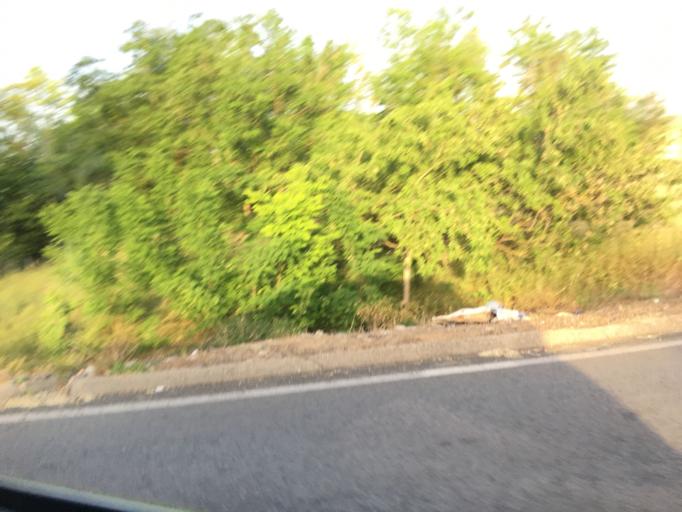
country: IT
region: Apulia
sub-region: Provincia di Lecce
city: Lequile
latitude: 40.3049
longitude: 18.1339
